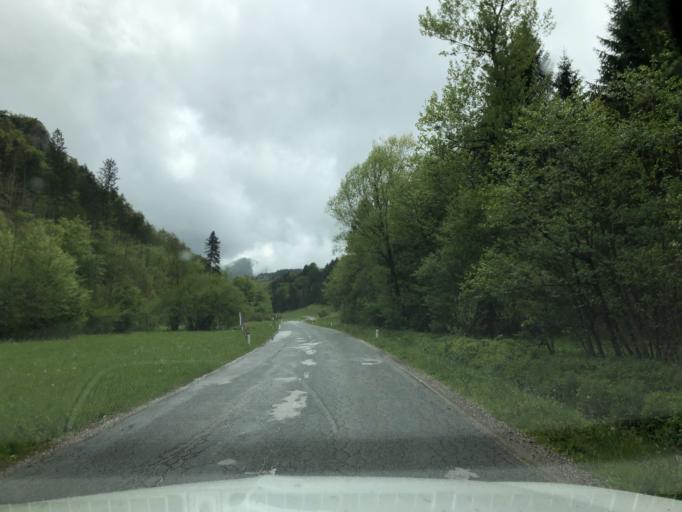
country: SI
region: Gorje
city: Zgornje Gorje
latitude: 46.4030
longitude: 14.0776
